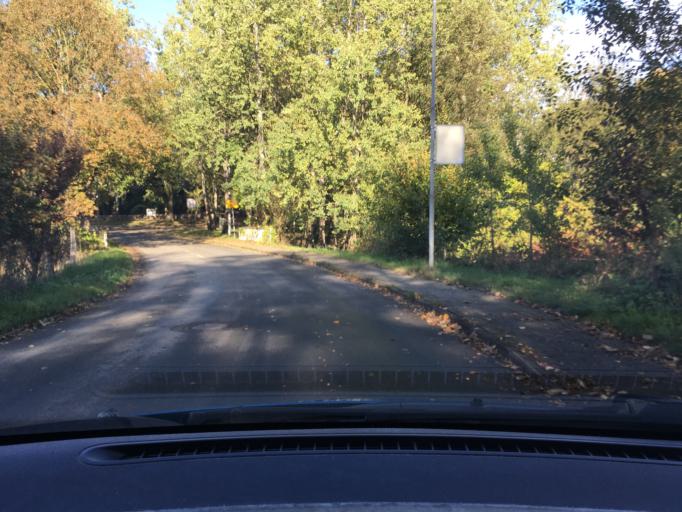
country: DE
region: Lower Saxony
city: Kakenstorf
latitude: 53.3091
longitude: 9.7885
